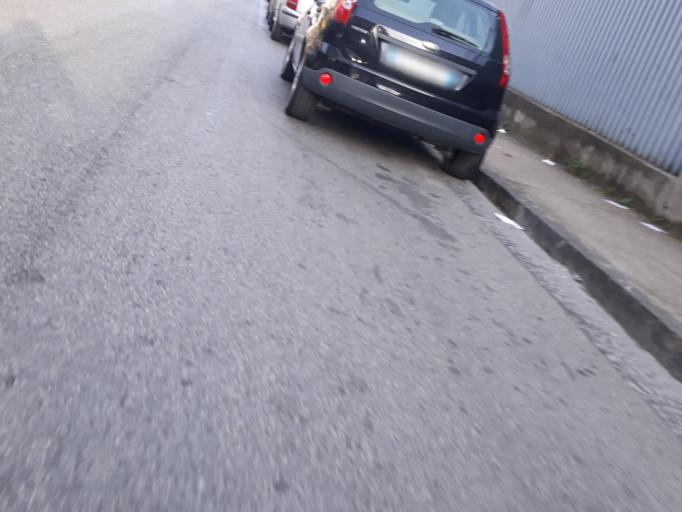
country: IT
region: Campania
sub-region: Provincia di Napoli
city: Napoli
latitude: 40.8554
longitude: 14.2831
